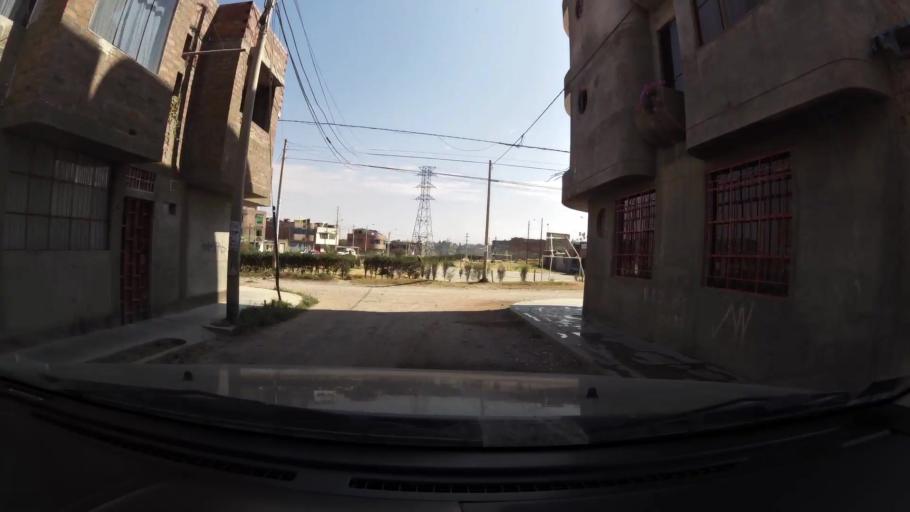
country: PE
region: Junin
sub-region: Provincia de Huancayo
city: El Tambo
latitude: -12.0731
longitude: -75.2289
